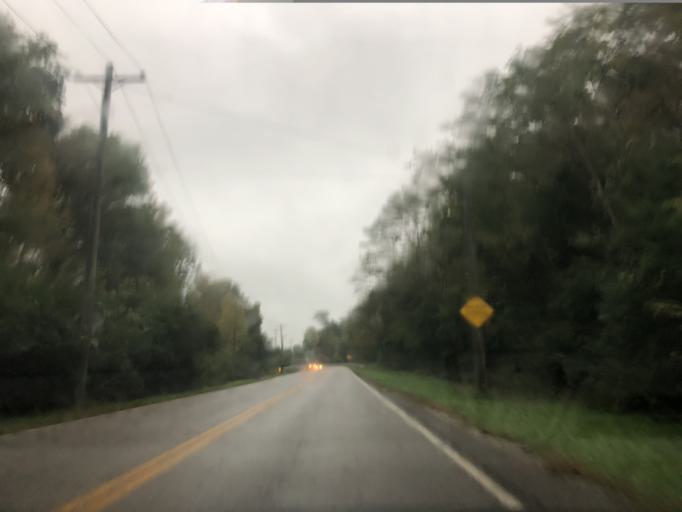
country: US
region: Ohio
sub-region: Hamilton County
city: The Village of Indian Hill
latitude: 39.2252
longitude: -84.2756
